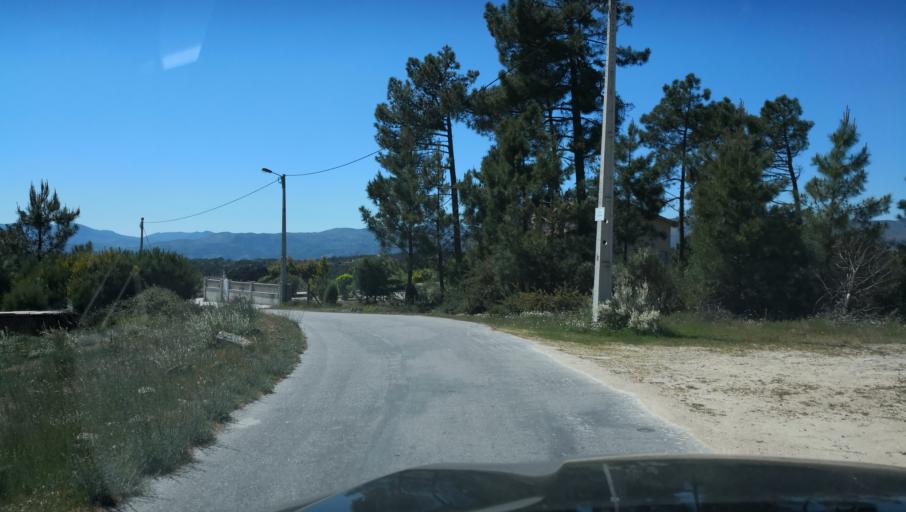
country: PT
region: Vila Real
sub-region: Sabrosa
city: Sabrosa
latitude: 41.2996
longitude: -7.6538
